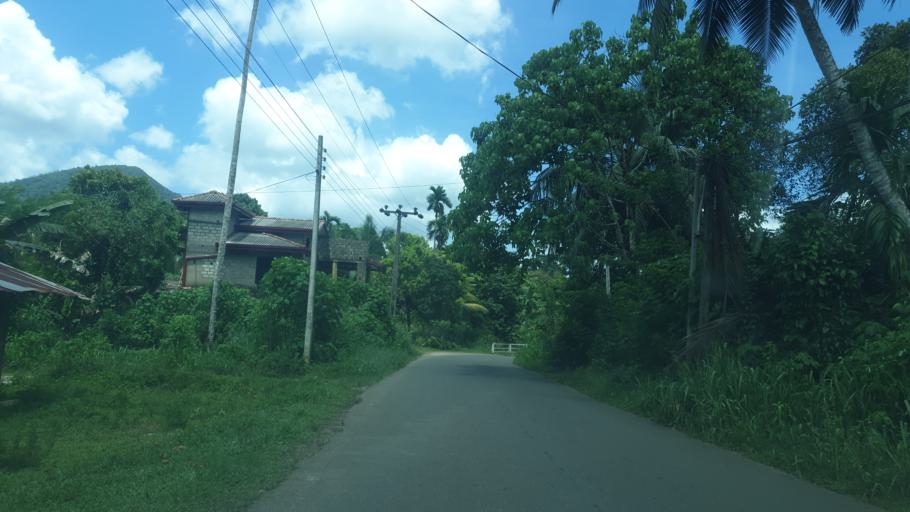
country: LK
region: Sabaragamuwa
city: Ratnapura
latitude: 6.4938
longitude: 80.3965
